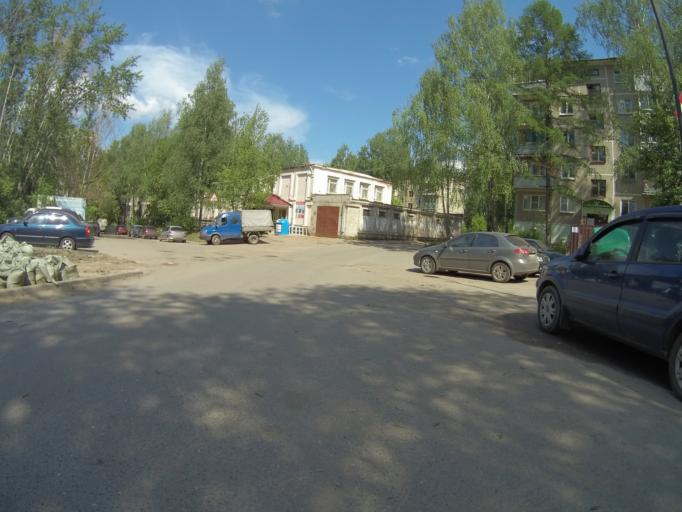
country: RU
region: Vladimir
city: Vladimir
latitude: 56.1314
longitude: 40.3539
